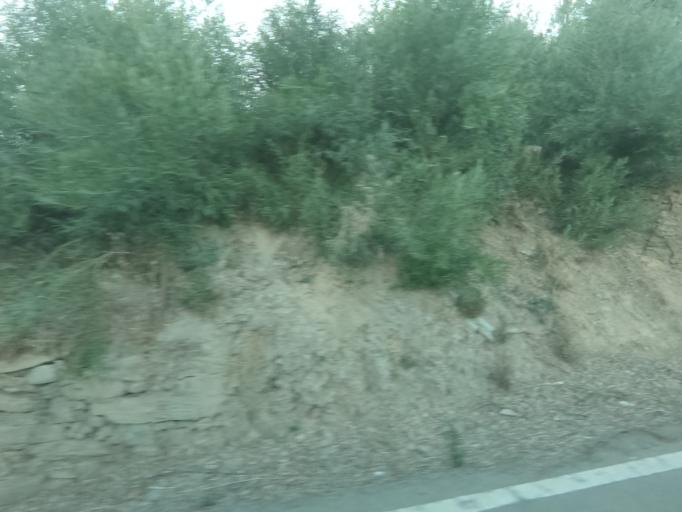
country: PT
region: Vila Real
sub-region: Mesao Frio
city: Mesao Frio
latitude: 41.1957
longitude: -7.8614
